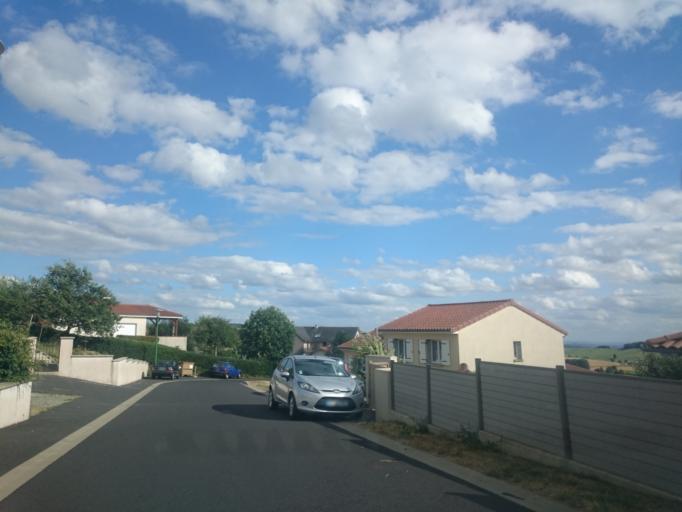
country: FR
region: Auvergne
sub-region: Departement du Cantal
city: Saint-Mamet-la-Salvetat
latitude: 44.8591
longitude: 2.3036
